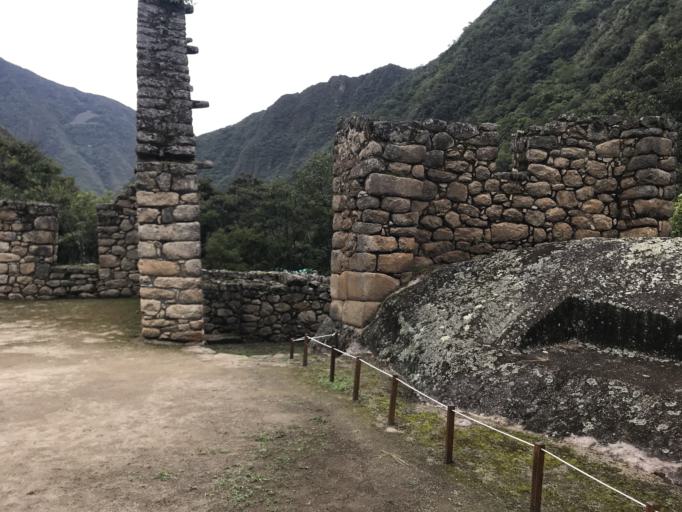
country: PE
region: Cusco
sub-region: Provincia de La Convencion
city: Santa Teresa
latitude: -13.1864
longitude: -72.5103
